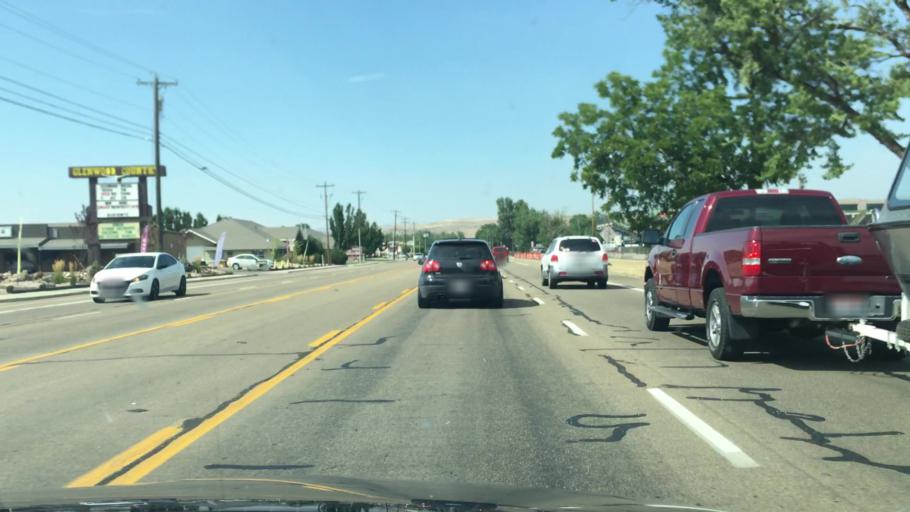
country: US
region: Idaho
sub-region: Ada County
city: Garden City
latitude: 43.6538
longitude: -116.2797
